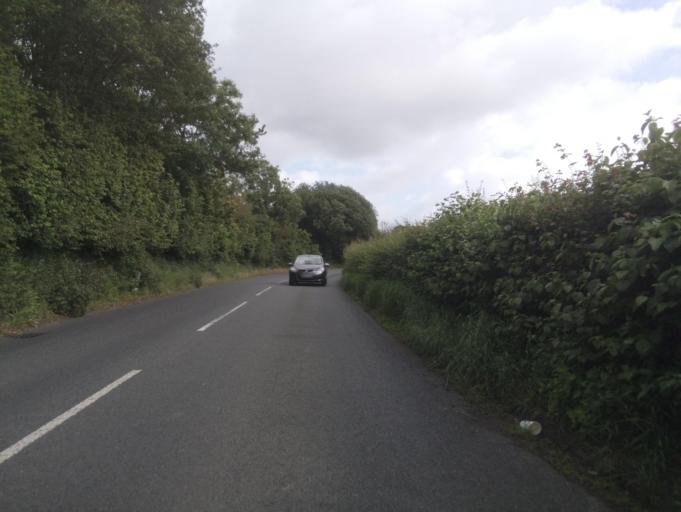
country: GB
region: England
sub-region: Bath and North East Somerset
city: Corston
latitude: 51.4084
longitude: -2.4341
